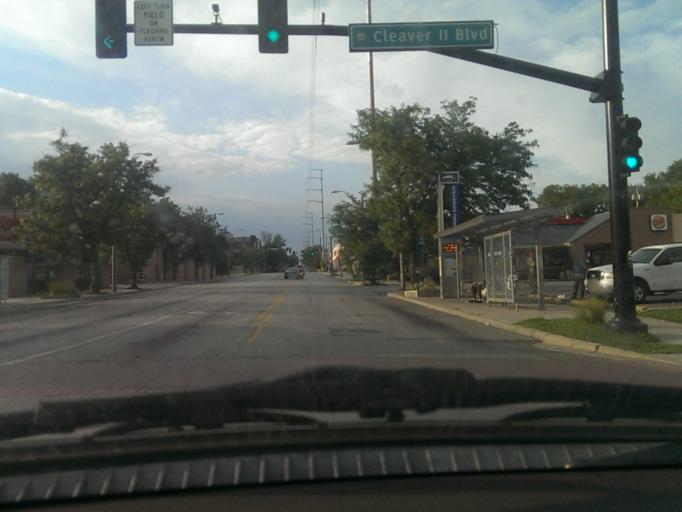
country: US
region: Kansas
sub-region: Johnson County
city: Westwood
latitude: 39.0416
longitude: -94.5729
